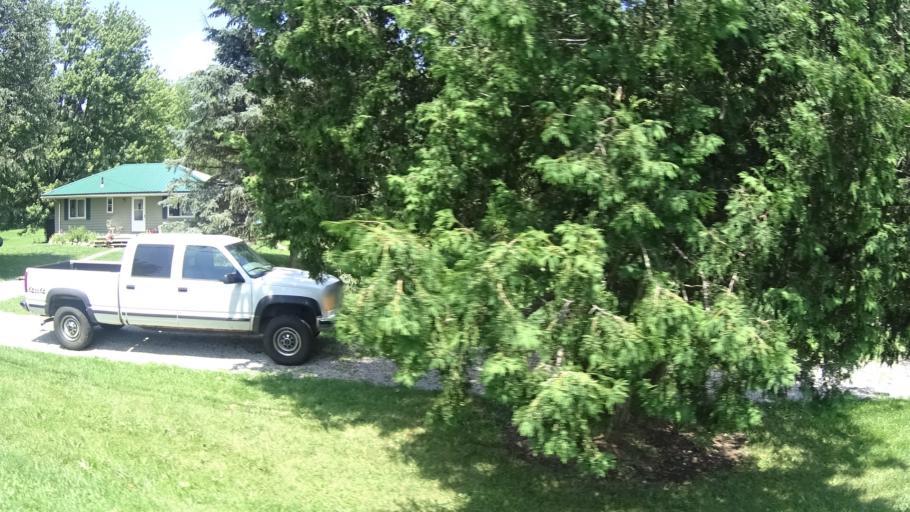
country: US
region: Ohio
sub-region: Lorain County
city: Vermilion
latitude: 41.3616
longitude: -82.3455
